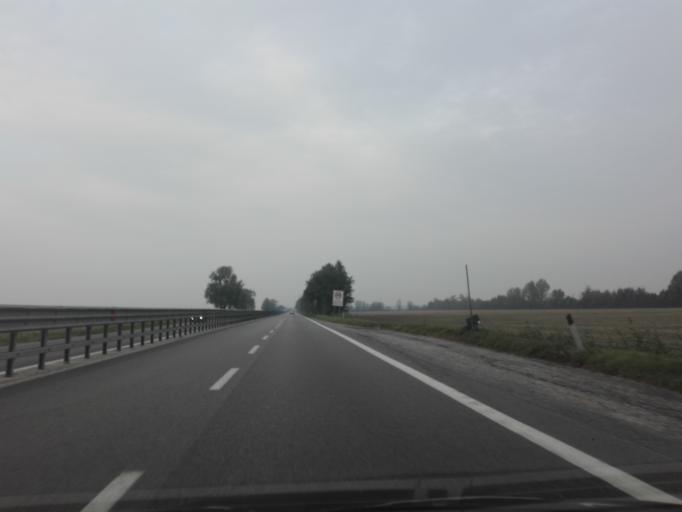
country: IT
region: Veneto
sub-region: Provincia di Rovigo
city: Pincara
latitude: 45.0236
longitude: 11.6186
